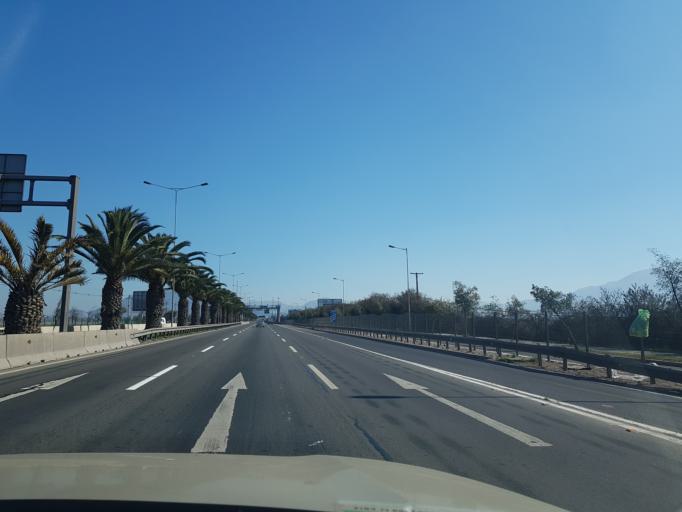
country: CL
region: Santiago Metropolitan
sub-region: Provincia de Santiago
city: Lo Prado
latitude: -33.3978
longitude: -70.7737
